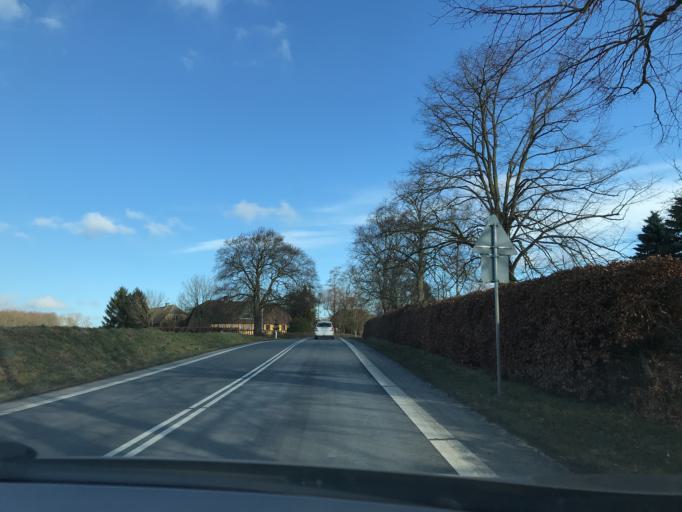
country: DK
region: South Denmark
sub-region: Middelfart Kommune
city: Brenderup
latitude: 55.4965
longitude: 9.9916
